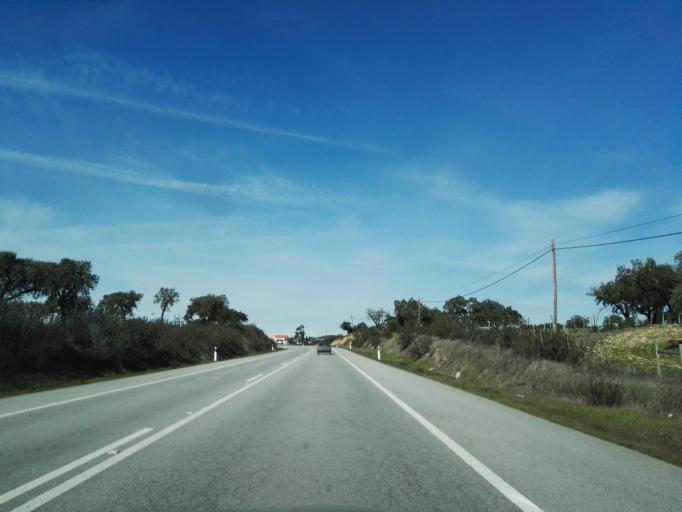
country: PT
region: Portalegre
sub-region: Portalegre
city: Urra
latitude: 39.2025
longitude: -7.3661
